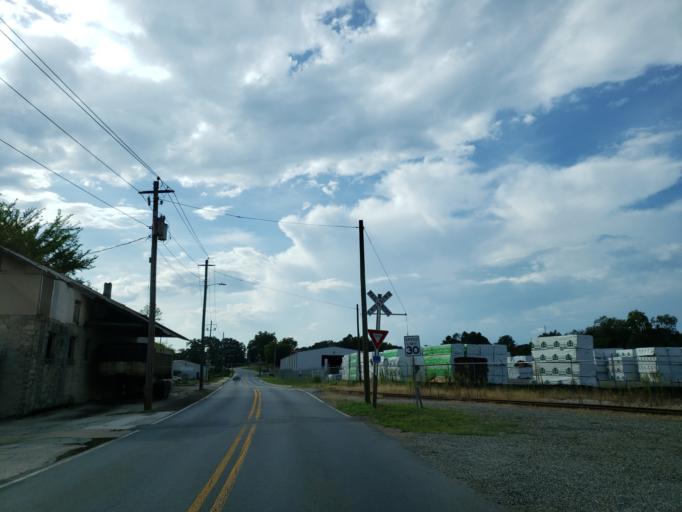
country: US
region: Georgia
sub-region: Bartow County
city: Cartersville
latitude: 34.1745
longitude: -84.8024
